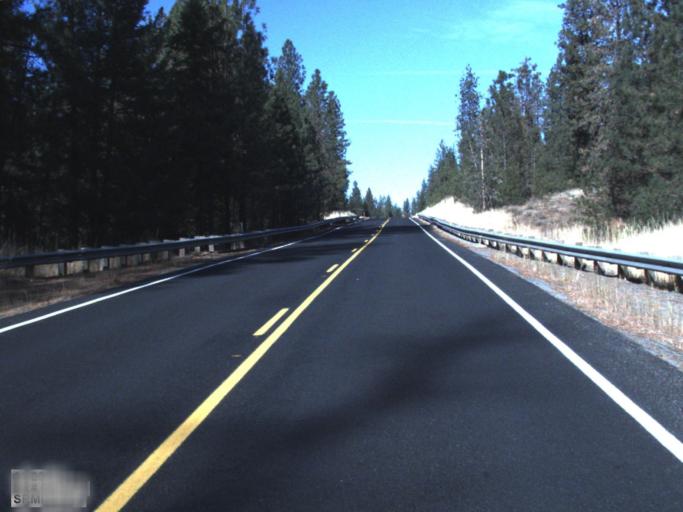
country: US
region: Washington
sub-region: Lincoln County
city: Davenport
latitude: 48.0322
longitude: -118.2311
